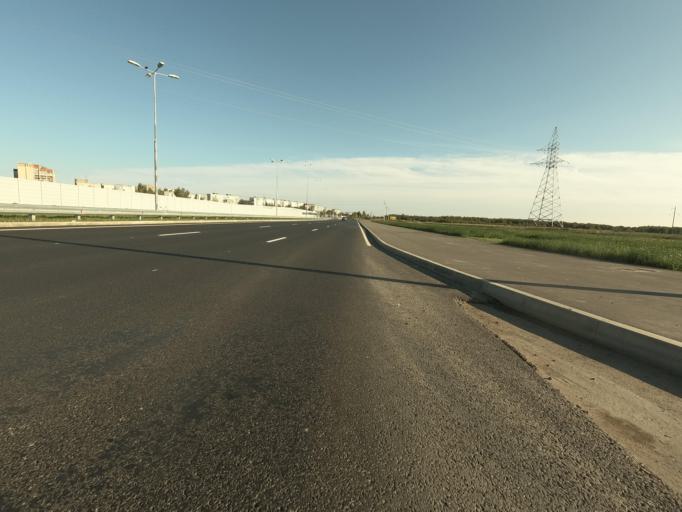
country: RU
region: St.-Petersburg
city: Kolpino
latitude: 59.7386
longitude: 30.5518
